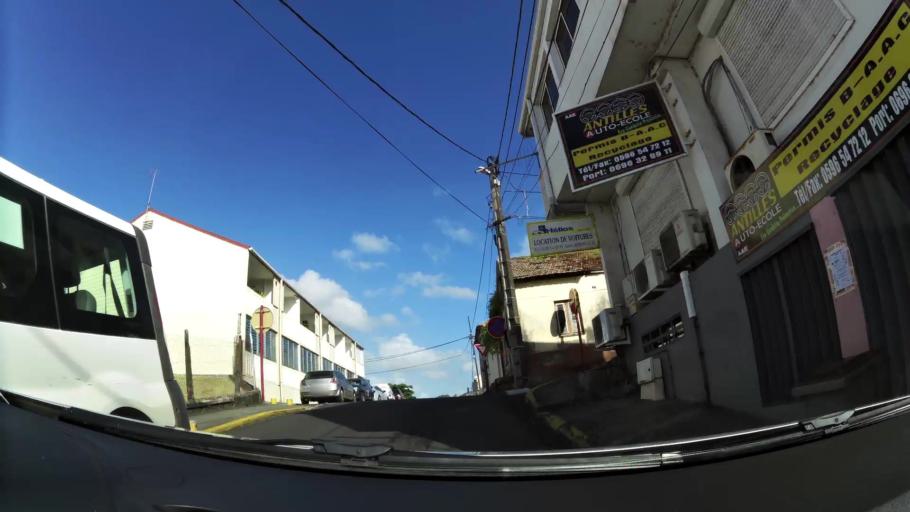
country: MQ
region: Martinique
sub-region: Martinique
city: Le Francois
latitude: 14.6141
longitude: -60.9047
